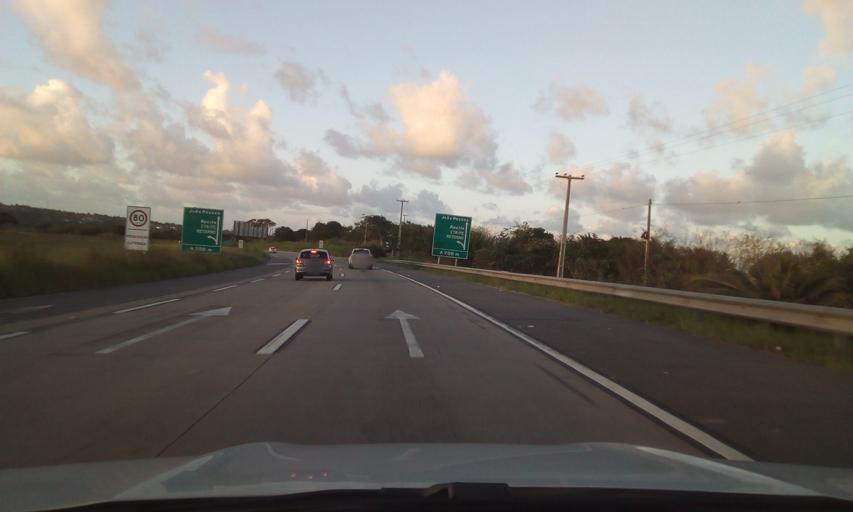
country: BR
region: Pernambuco
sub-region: Itapissuma
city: Itapissuma
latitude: -7.7025
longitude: -34.9231
